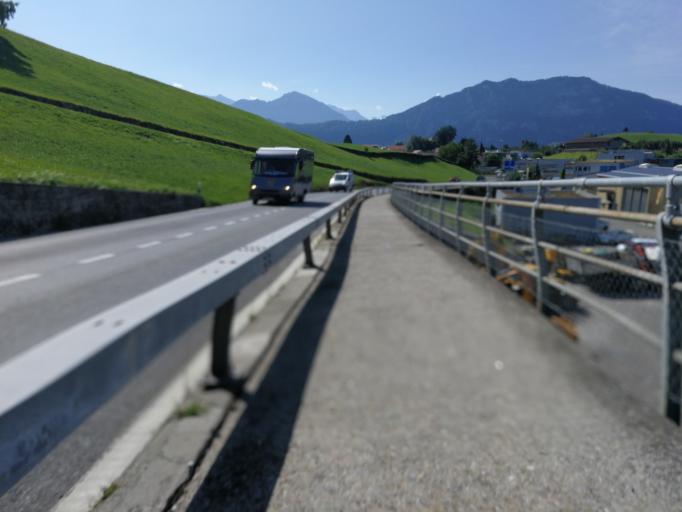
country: CH
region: Lucerne
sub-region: Lucerne-Land District
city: Weggis
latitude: 47.0385
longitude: 8.4216
